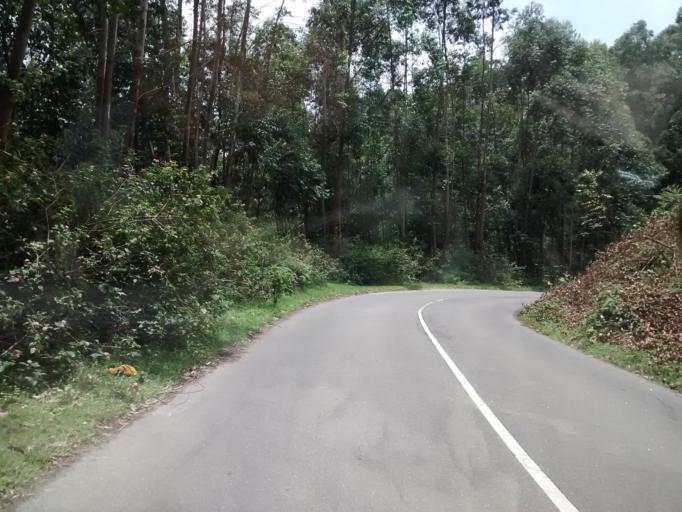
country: IN
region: Kerala
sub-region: Idukki
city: Munnar
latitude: 10.1238
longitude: 77.1595
